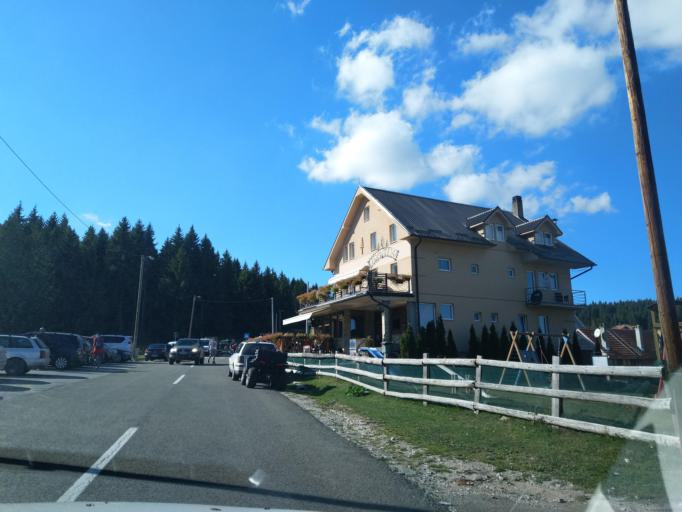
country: RS
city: Sokolovica
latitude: 43.2778
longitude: 20.3394
